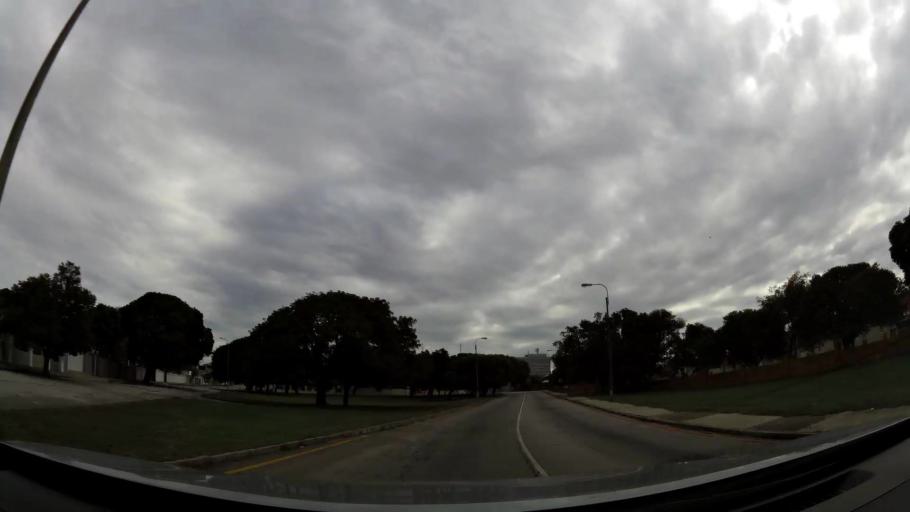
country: ZA
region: Eastern Cape
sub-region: Nelson Mandela Bay Metropolitan Municipality
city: Port Elizabeth
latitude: -33.9582
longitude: 25.5979
